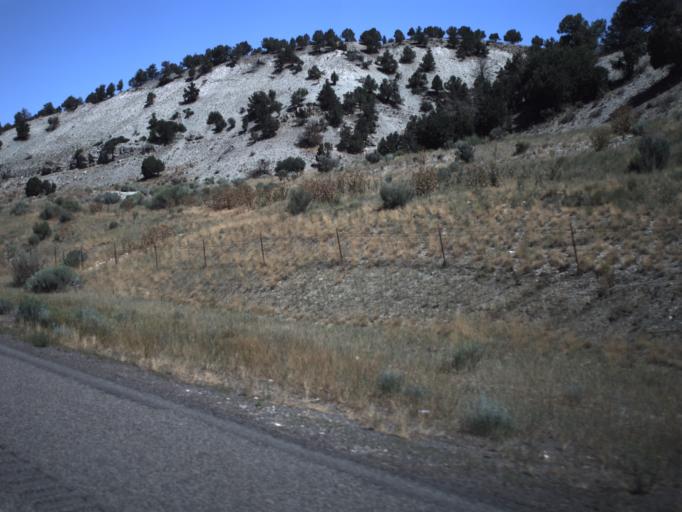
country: US
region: Utah
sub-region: Utah County
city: Mapleton
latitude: 39.9602
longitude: -111.3040
